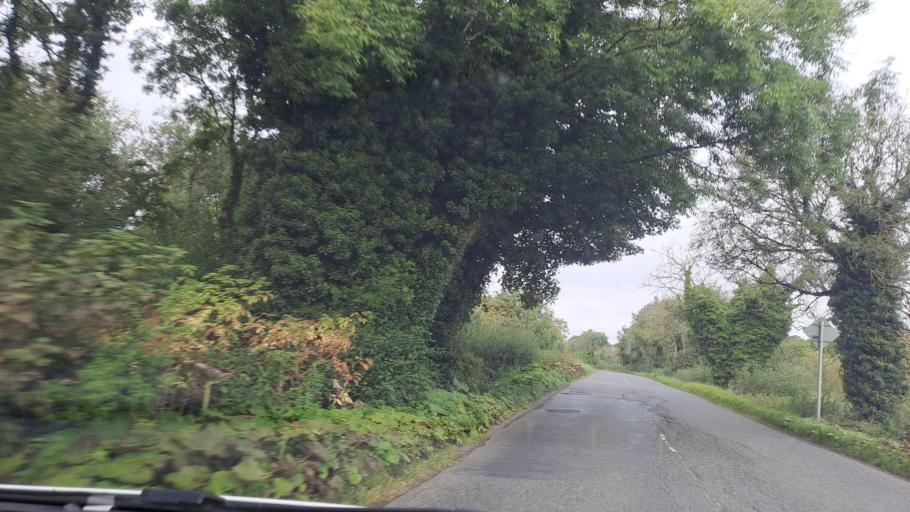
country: IE
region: Ulster
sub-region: An Cabhan
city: Kingscourt
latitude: 53.8839
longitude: -6.7371
